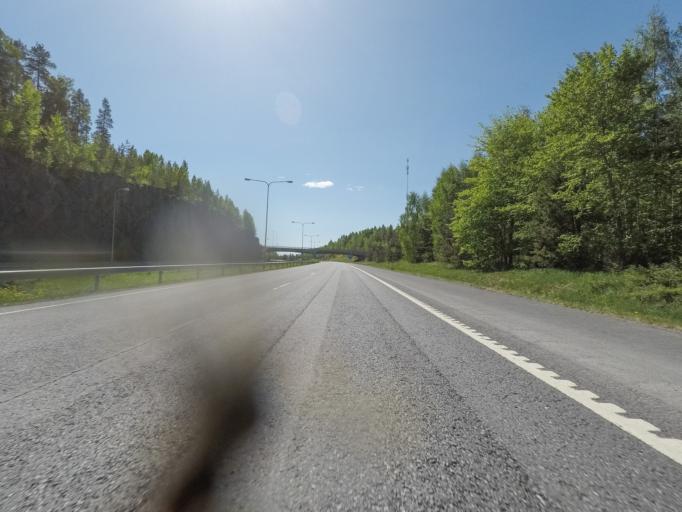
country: FI
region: Pirkanmaa
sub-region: Etelae-Pirkanmaa
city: Toijala
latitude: 61.1979
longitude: 23.8196
